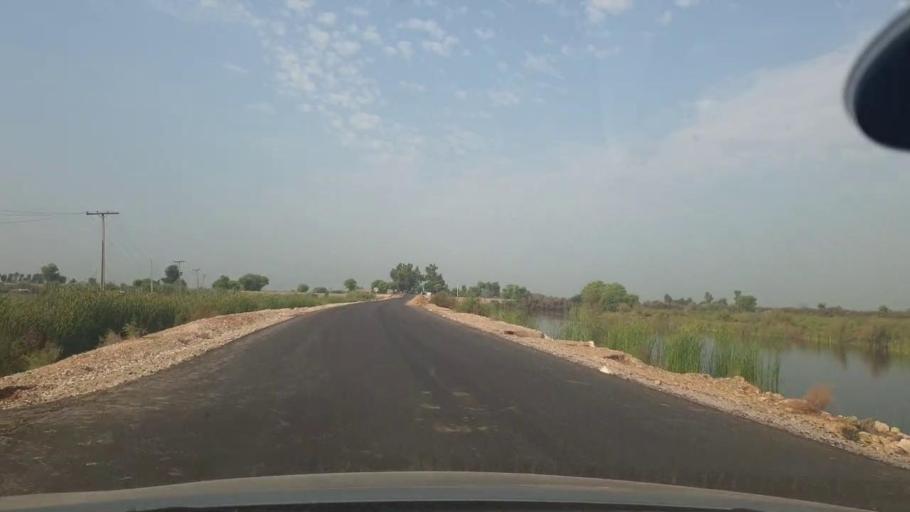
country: PK
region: Sindh
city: Jacobabad
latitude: 28.0934
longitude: 68.3283
